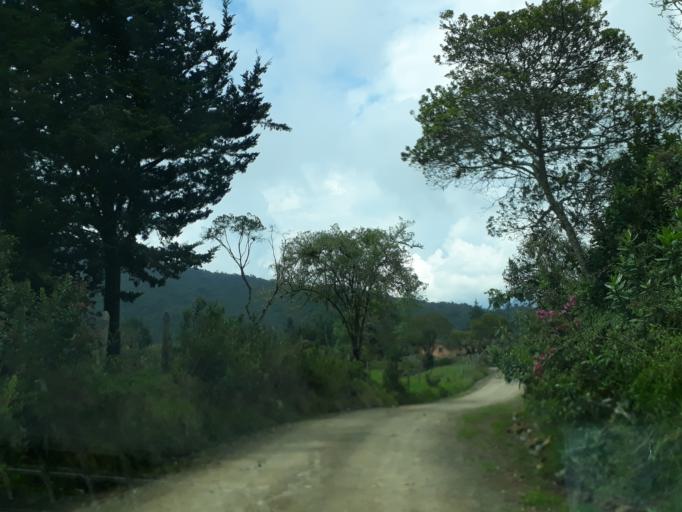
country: CO
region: Cundinamarca
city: Macheta
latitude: 5.1059
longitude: -73.5402
